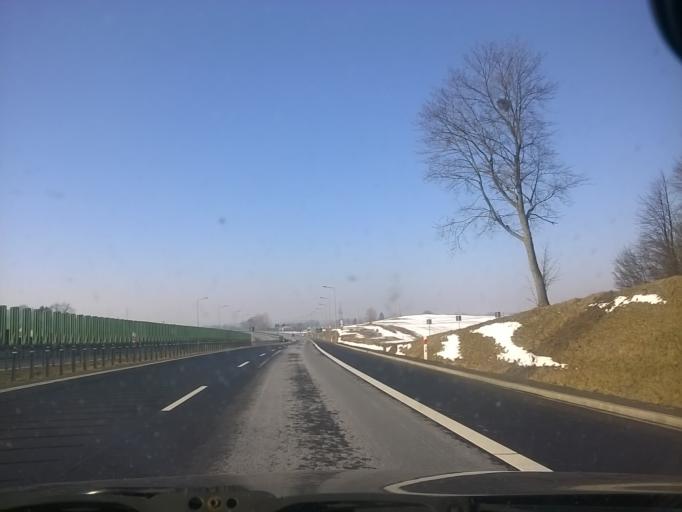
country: PL
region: Warmian-Masurian Voivodeship
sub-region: Powiat olsztynski
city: Biskupiec
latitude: 53.8473
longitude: 20.9791
